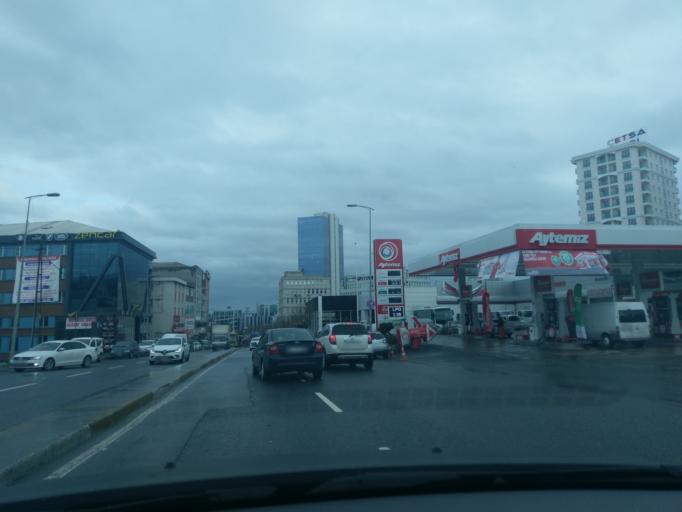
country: TR
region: Istanbul
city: Mahmutbey
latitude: 41.0598
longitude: 28.8317
